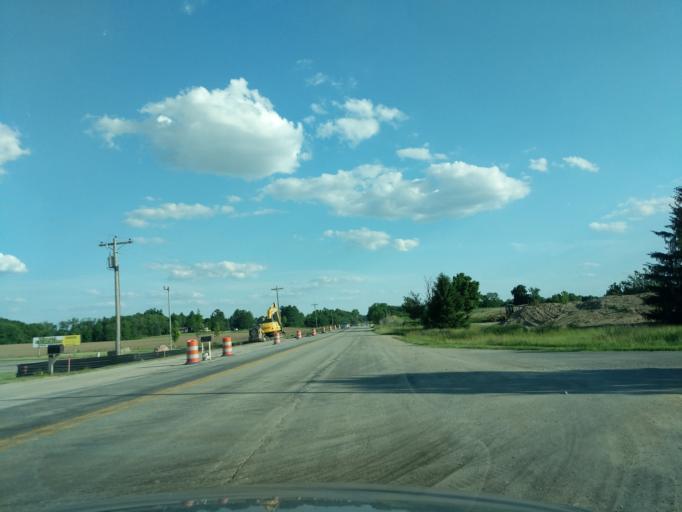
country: US
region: Indiana
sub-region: Whitley County
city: Columbia City
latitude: 41.1373
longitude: -85.4814
